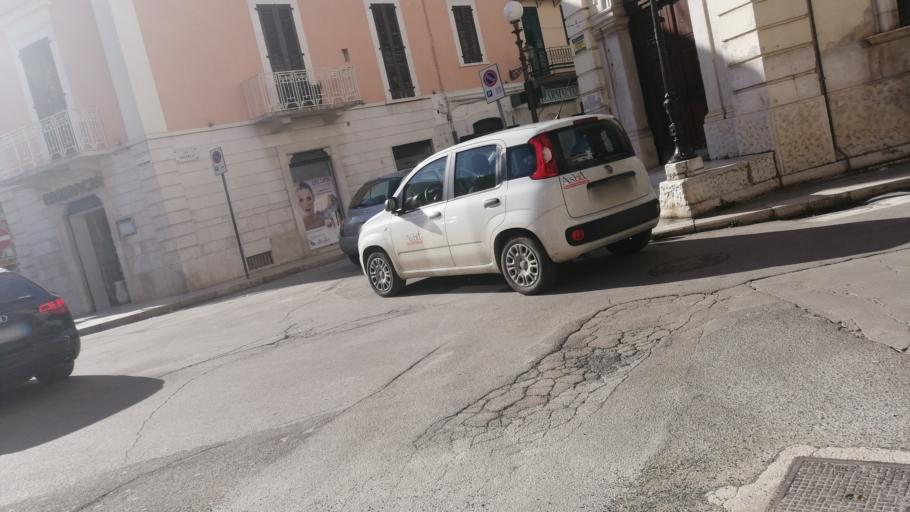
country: IT
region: Apulia
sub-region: Provincia di Barletta - Andria - Trani
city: Andria
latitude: 41.2234
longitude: 16.2932
